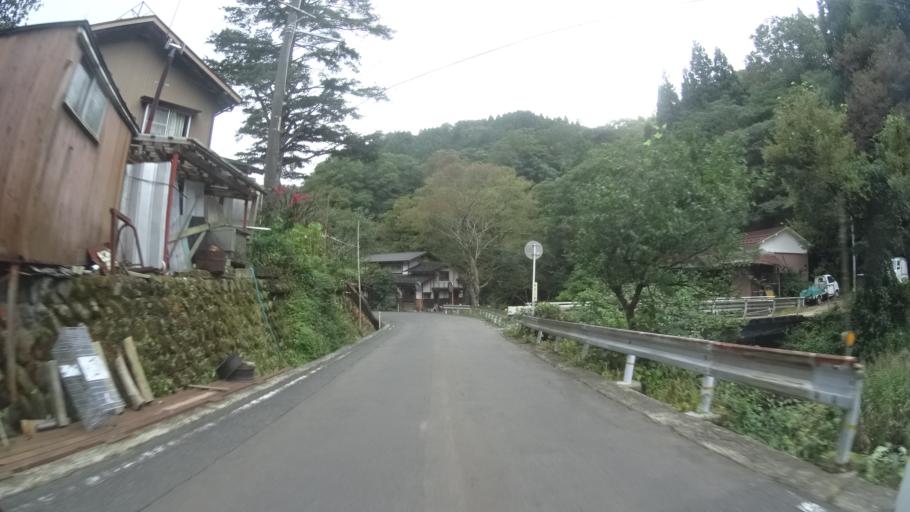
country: JP
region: Tottori
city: Kurayoshi
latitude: 35.4040
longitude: 133.9723
